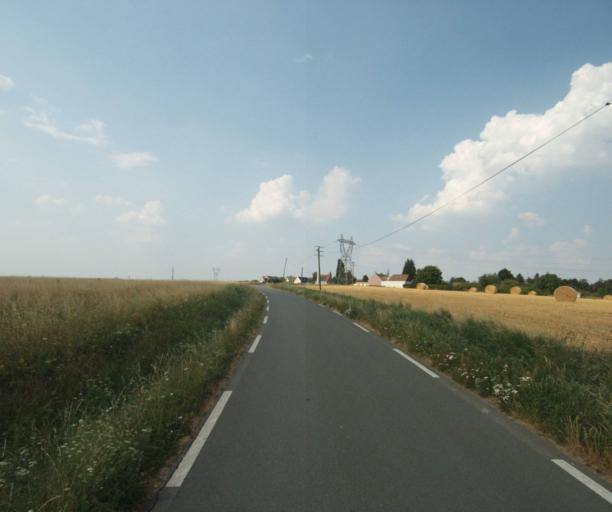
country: FR
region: Nord-Pas-de-Calais
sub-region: Departement du Nord
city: Linselles
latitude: 50.7287
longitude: 3.0744
